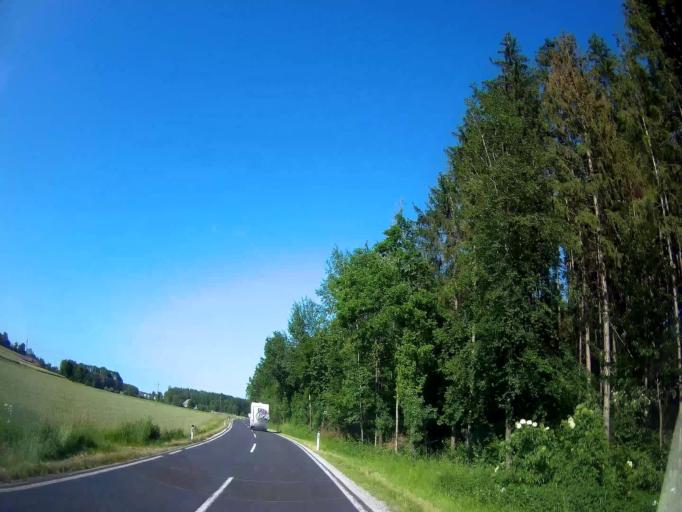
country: AT
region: Upper Austria
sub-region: Politischer Bezirk Braunau am Inn
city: Braunau am Inn
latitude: 48.1563
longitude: 13.0443
